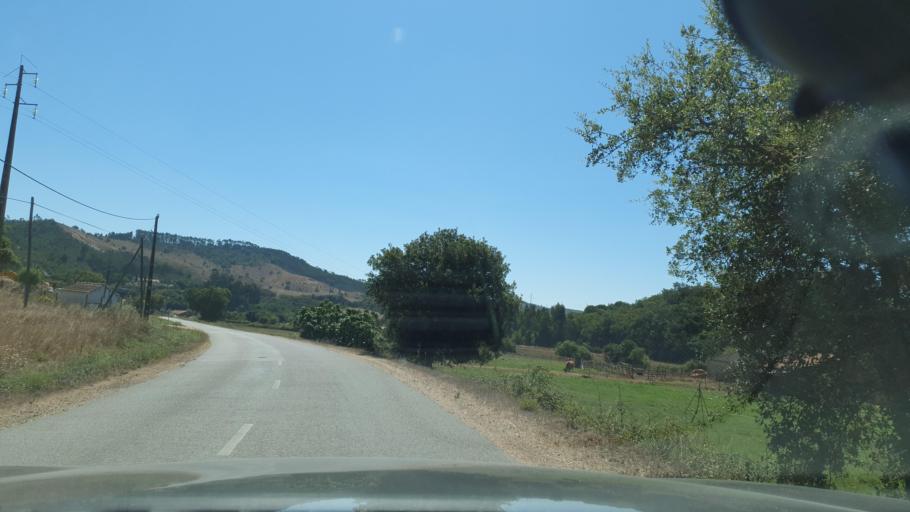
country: PT
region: Beja
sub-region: Odemira
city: Sao Teotonio
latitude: 37.4952
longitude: -8.6486
